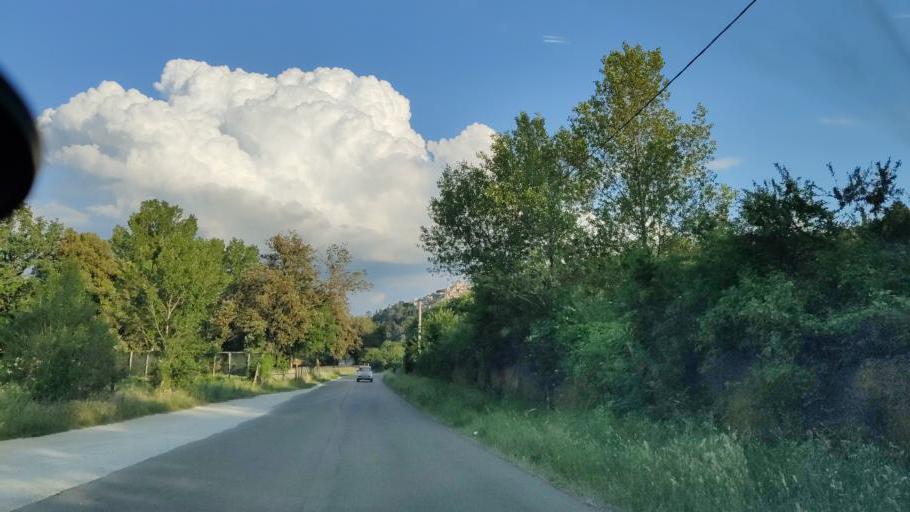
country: IT
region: Umbria
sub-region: Provincia di Terni
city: Amelia
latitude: 42.5692
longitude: 12.4066
